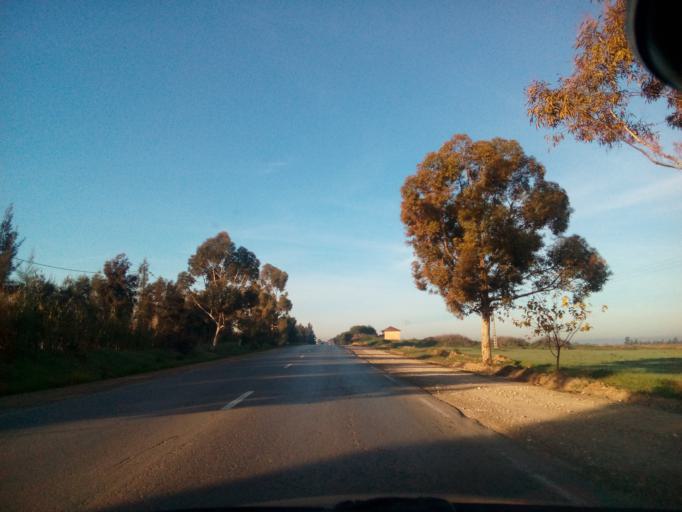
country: DZ
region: Relizane
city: Relizane
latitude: 35.7284
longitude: 0.4084
